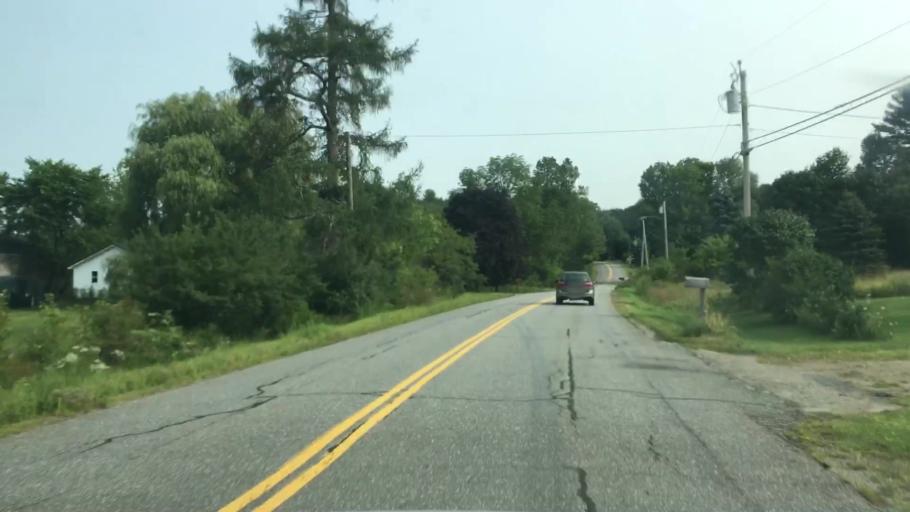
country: US
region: Maine
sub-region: Kennebec County
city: Chelsea
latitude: 44.2935
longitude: -69.6979
